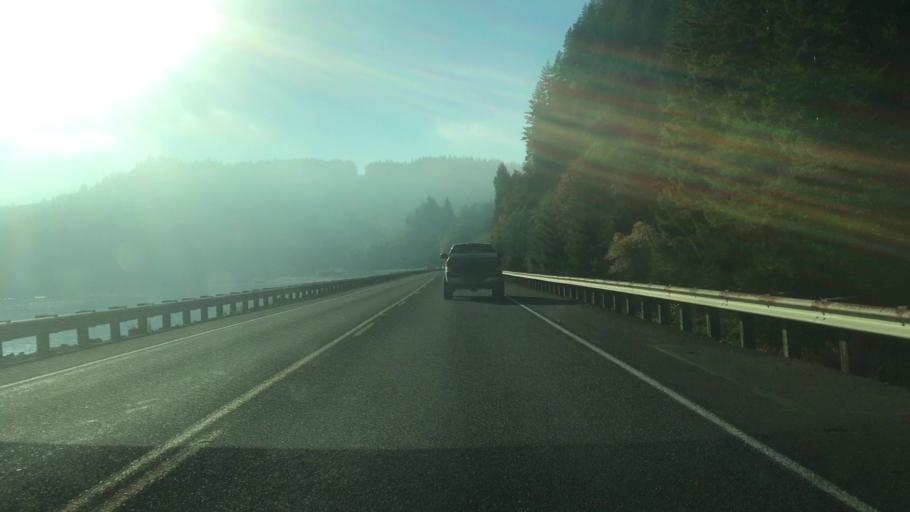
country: US
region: Oregon
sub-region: Clatsop County
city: Astoria
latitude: 46.2617
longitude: -123.8435
